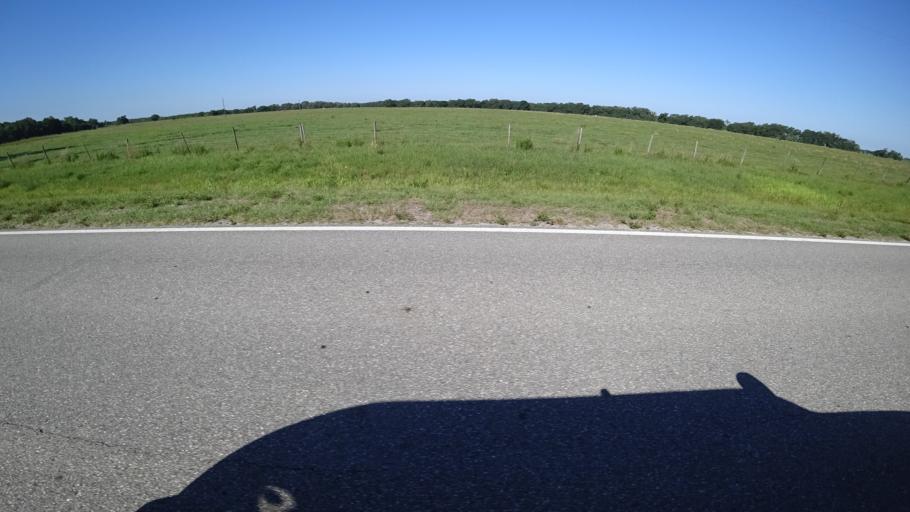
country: US
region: Florida
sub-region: Sarasota County
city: The Meadows
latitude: 27.5041
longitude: -82.3166
